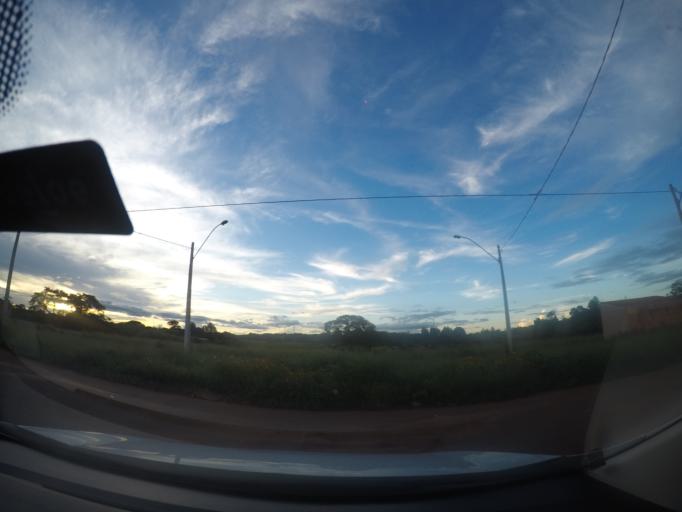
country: BR
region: Goias
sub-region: Goianira
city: Goianira
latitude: -16.5636
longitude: -49.3766
